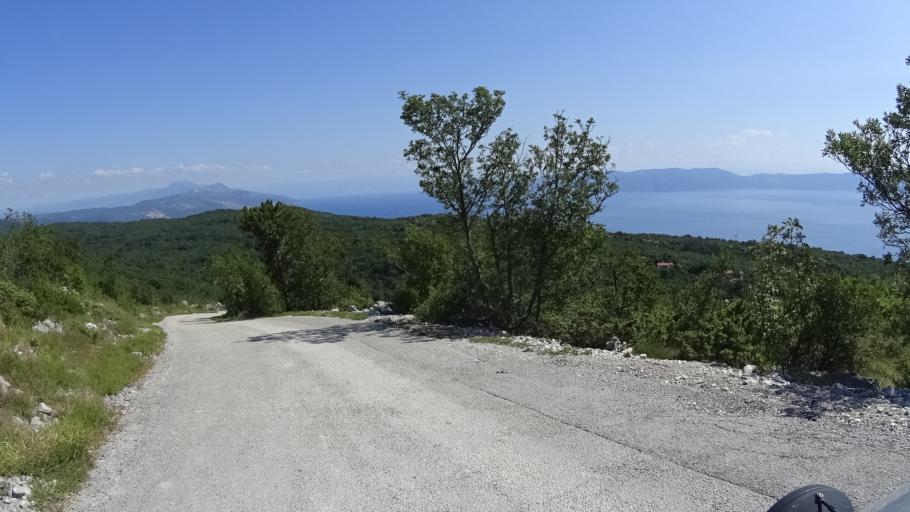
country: HR
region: Istarska
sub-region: Grad Labin
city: Rabac
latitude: 44.9893
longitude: 14.1461
